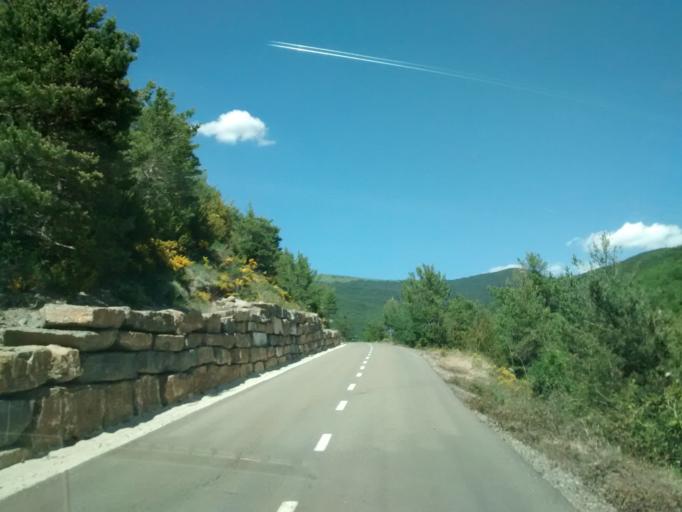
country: ES
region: Aragon
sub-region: Provincia de Huesca
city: Borau
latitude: 42.6672
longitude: -0.5946
